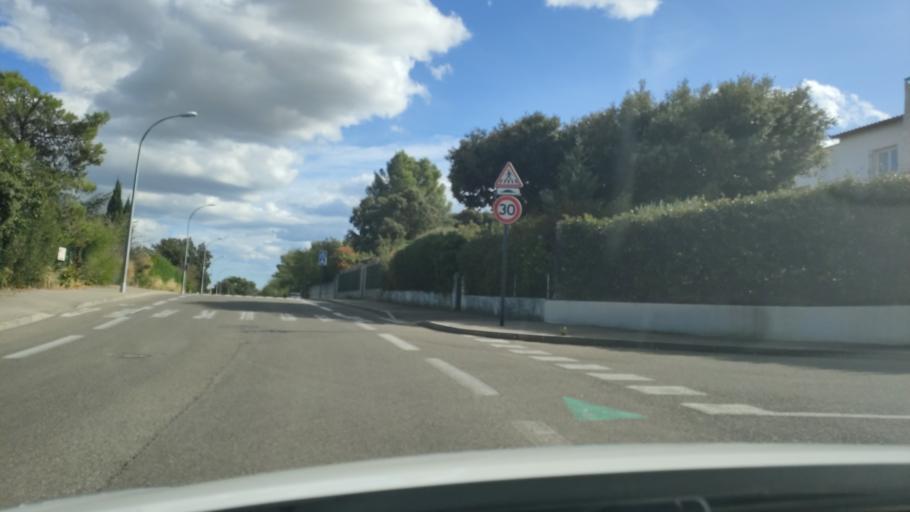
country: FR
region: Languedoc-Roussillon
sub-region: Departement du Gard
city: Villeneuve-les-Avignon
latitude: 43.9719
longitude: 4.7776
